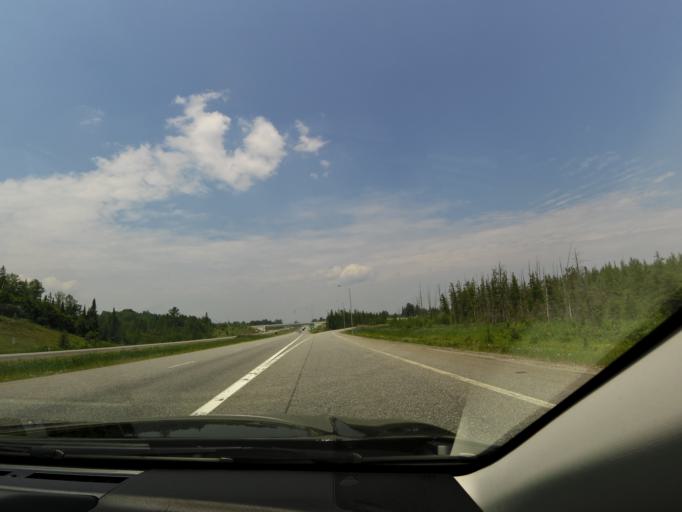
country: CA
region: Ontario
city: Huntsville
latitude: 45.5078
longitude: -79.3026
